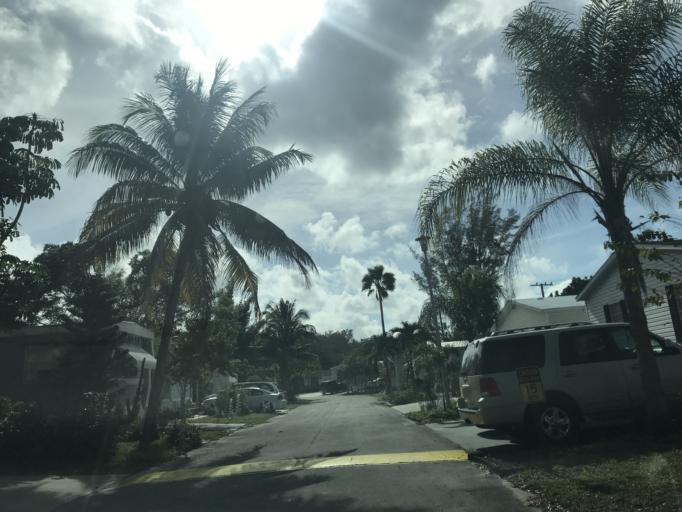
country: US
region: Florida
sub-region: Palm Beach County
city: Boca Pointe
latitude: 26.3103
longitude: -80.1766
